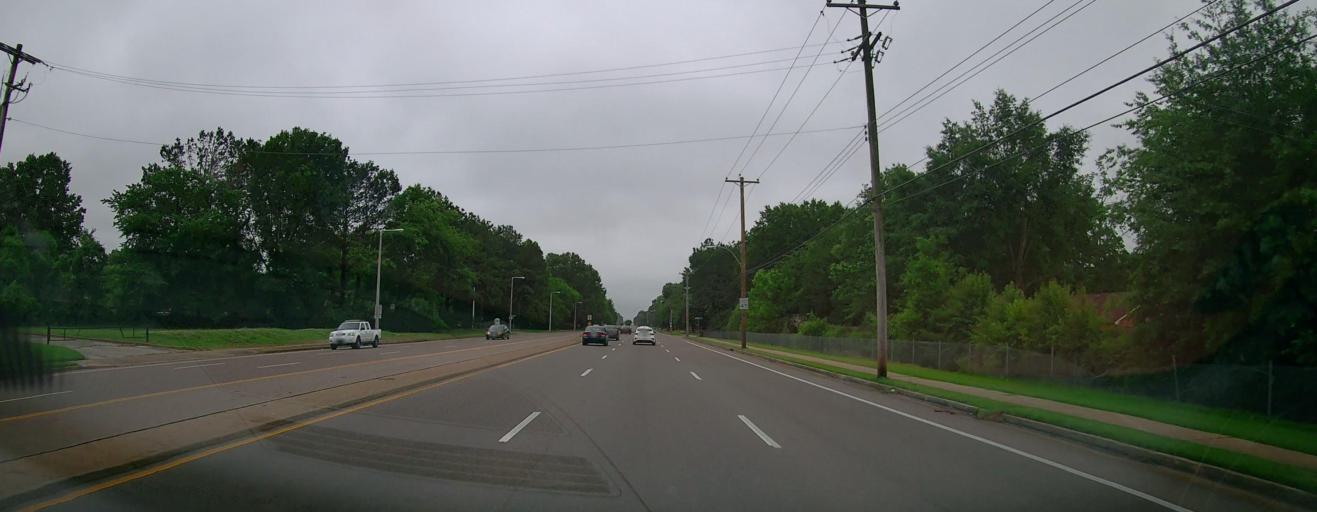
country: US
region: Mississippi
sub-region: De Soto County
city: Olive Branch
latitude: 35.0170
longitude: -89.8313
